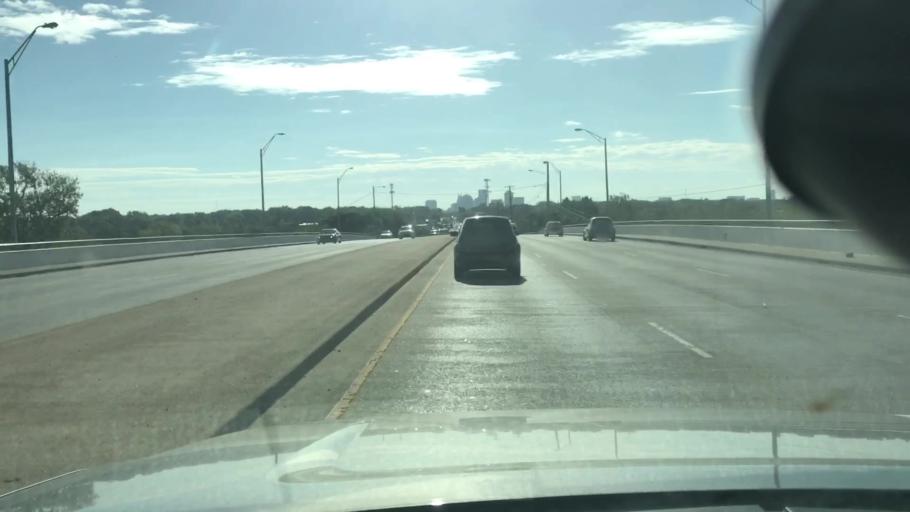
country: US
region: Tennessee
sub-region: Davidson County
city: Nashville
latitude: 36.1917
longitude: -86.8278
